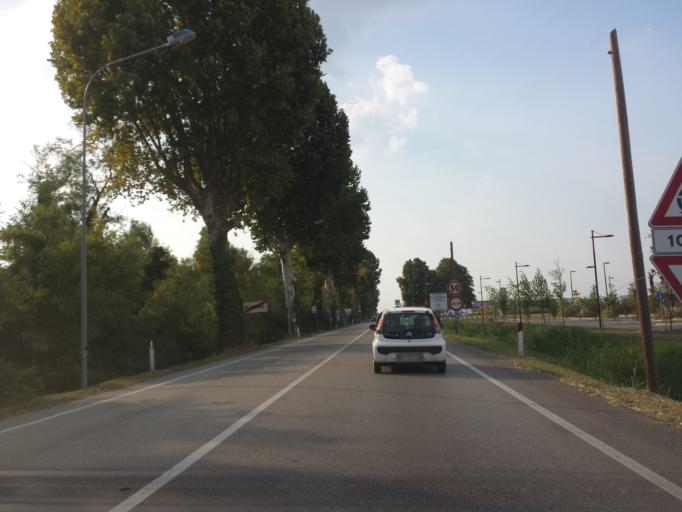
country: IT
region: Veneto
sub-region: Provincia di Padova
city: Rubano
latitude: 45.4303
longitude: 11.7792
